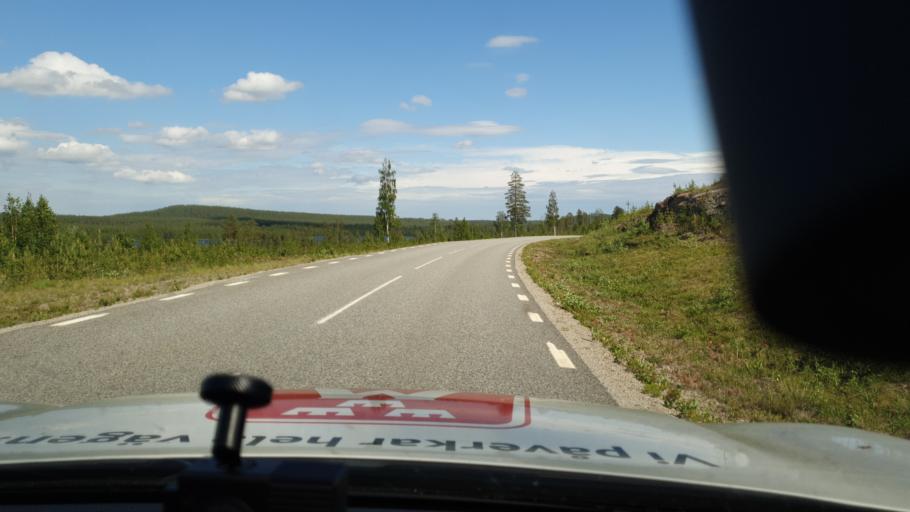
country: SE
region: Vaesterbotten
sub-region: Lycksele Kommun
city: Soderfors
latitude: 64.9372
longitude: 18.3061
